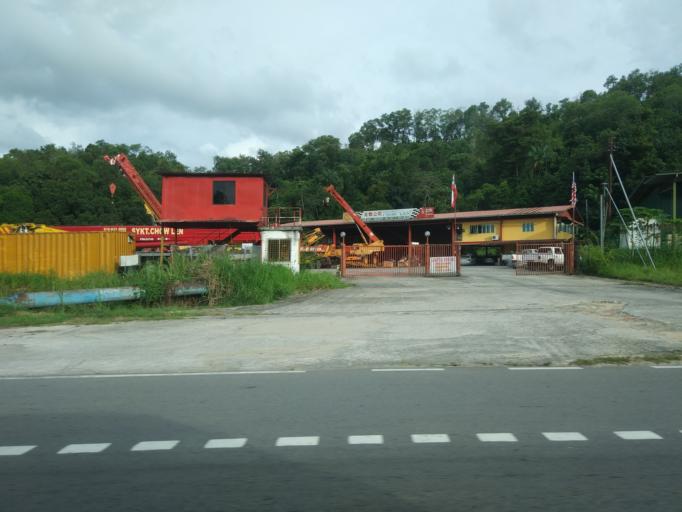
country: MY
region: Sabah
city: Kota Kinabalu
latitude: 6.0075
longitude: 116.1342
